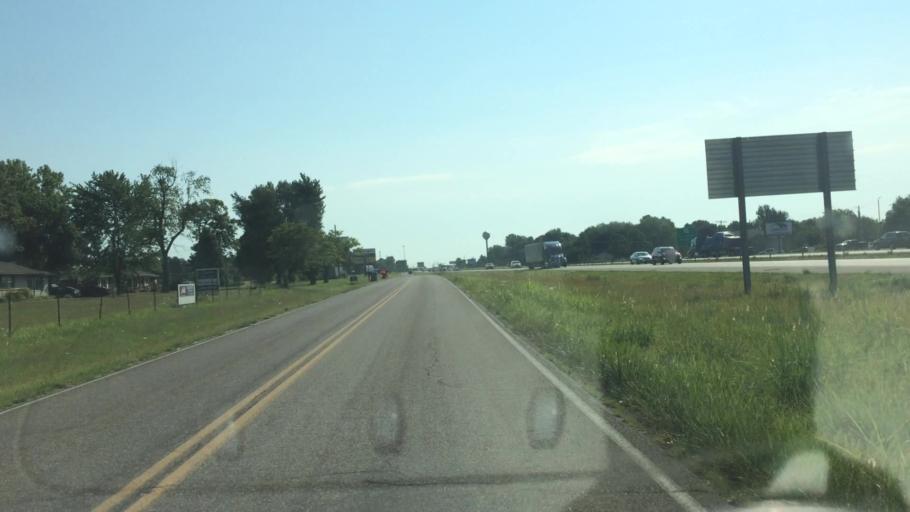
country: US
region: Missouri
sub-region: Greene County
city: Strafford
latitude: 37.2670
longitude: -93.1357
